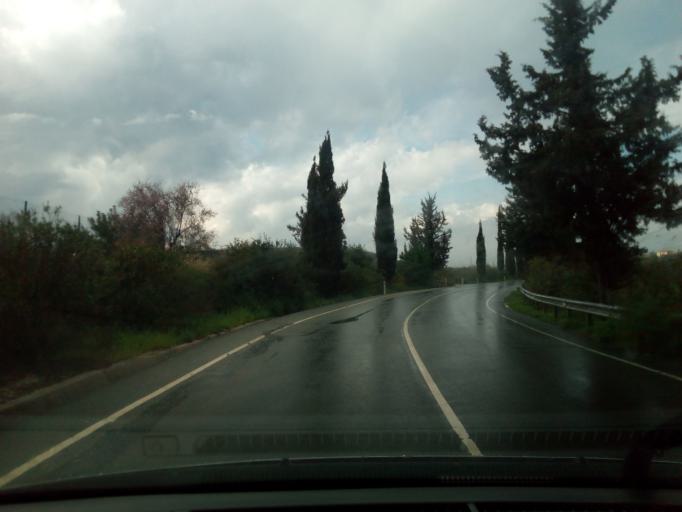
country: CY
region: Pafos
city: Polis
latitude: 35.0121
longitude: 32.4517
